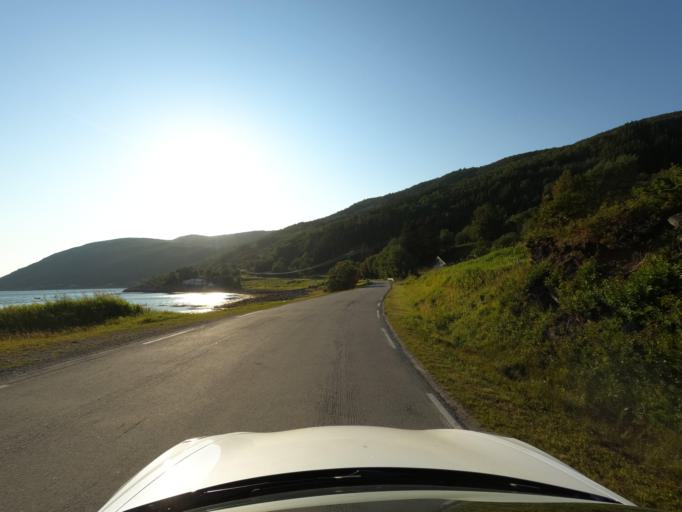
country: NO
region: Nordland
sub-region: Ballangen
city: Ballangen
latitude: 68.4676
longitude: 16.8126
